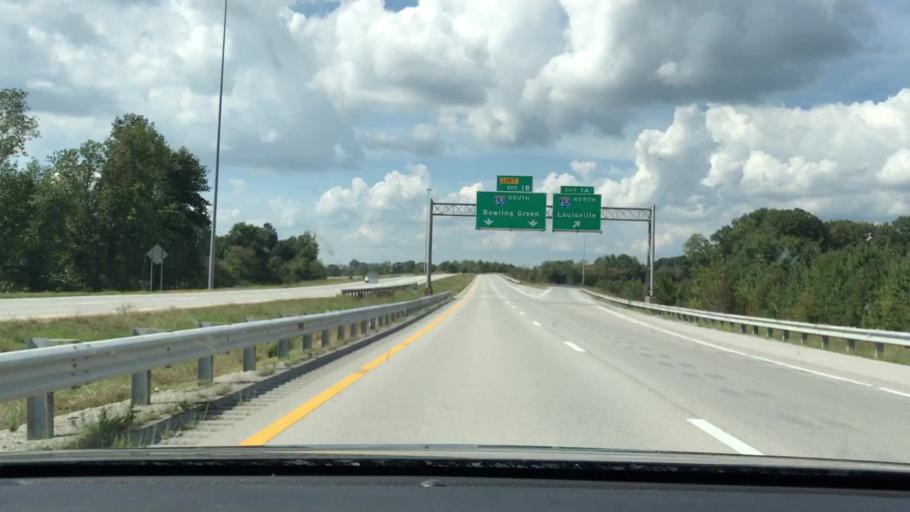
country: US
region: Kentucky
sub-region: Barren County
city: Cave City
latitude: 37.0557
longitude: -86.1070
